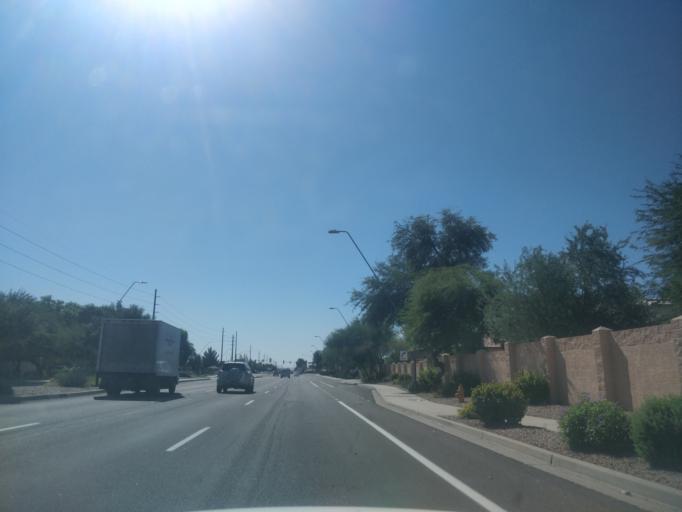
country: US
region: Arizona
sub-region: Maricopa County
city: Chandler
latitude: 33.2945
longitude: -111.8244
